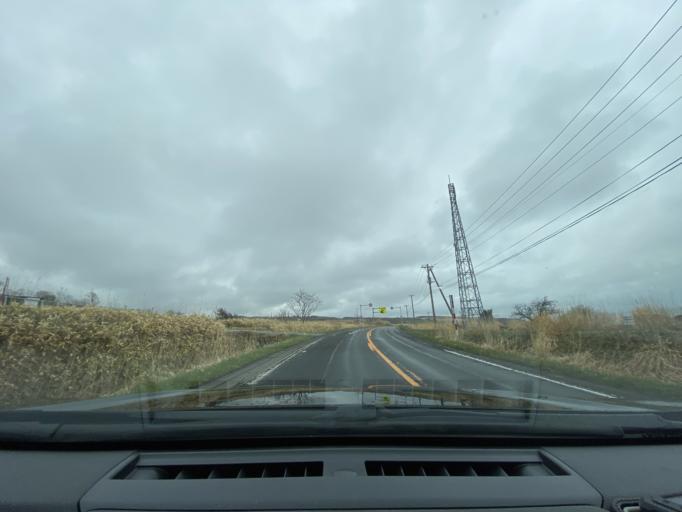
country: JP
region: Hokkaido
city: Ishikari
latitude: 43.3628
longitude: 141.4309
